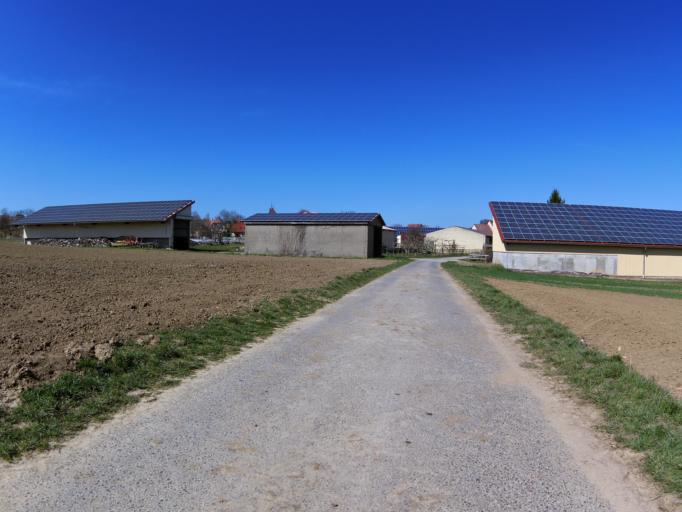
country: DE
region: Bavaria
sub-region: Regierungsbezirk Unterfranken
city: Prosselsheim
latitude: 49.8602
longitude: 10.1282
